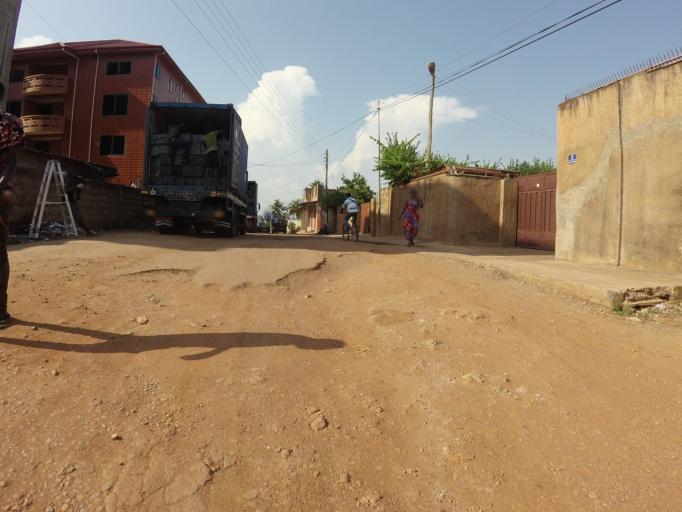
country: GH
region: Greater Accra
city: Dome
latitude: 5.6097
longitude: -0.2432
